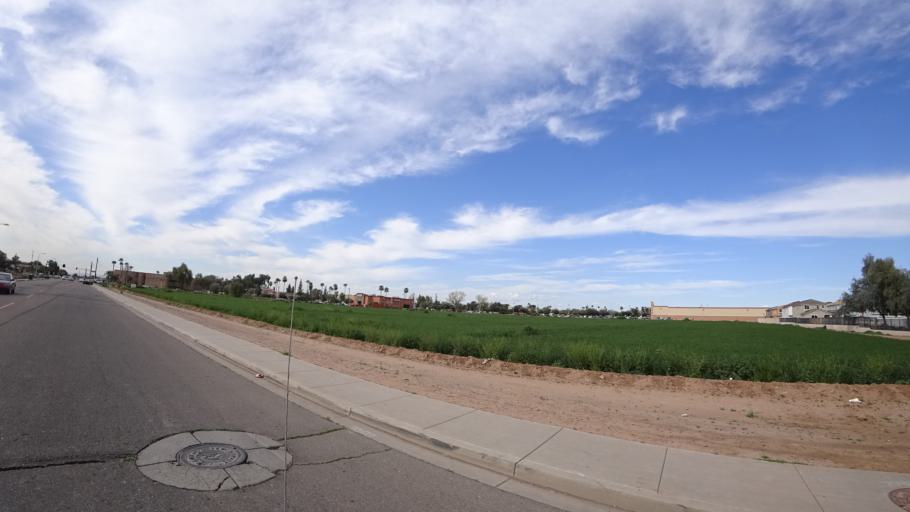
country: US
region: Arizona
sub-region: Maricopa County
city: Tolleson
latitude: 33.4730
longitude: -112.2183
